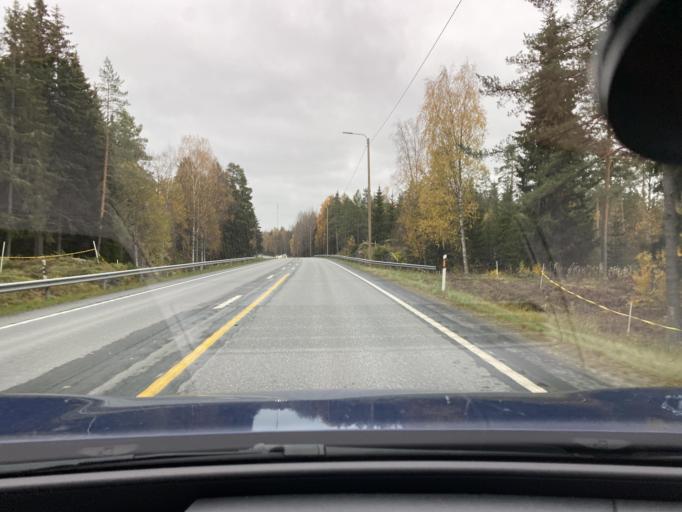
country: FI
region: Varsinais-Suomi
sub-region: Vakka-Suomi
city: Laitila
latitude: 60.9366
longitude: 21.6040
